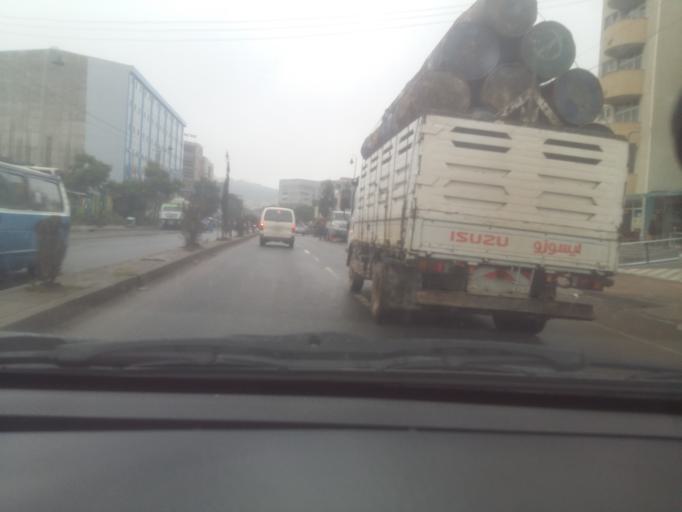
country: ET
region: Adis Abeba
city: Addis Ababa
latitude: 8.9508
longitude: 38.7185
